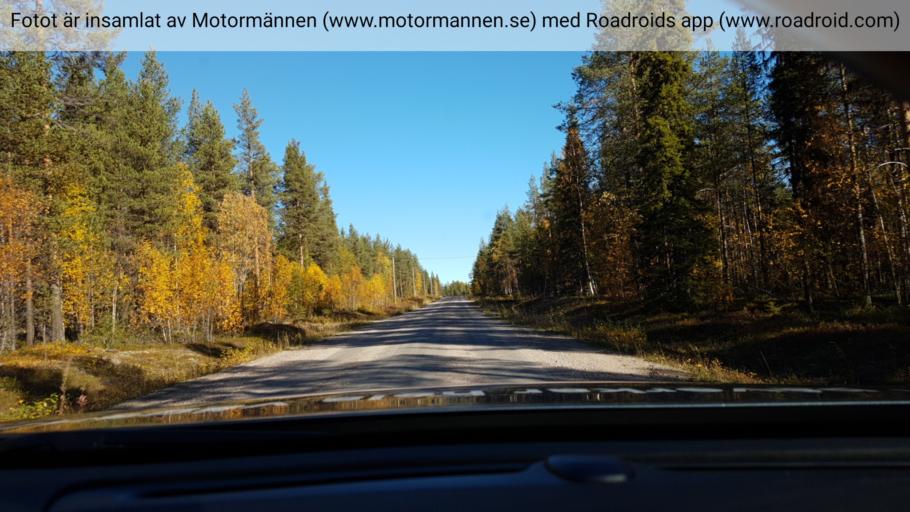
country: SE
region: Norrbotten
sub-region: Gallivare Kommun
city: Gaellivare
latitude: 66.5639
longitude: 21.0134
